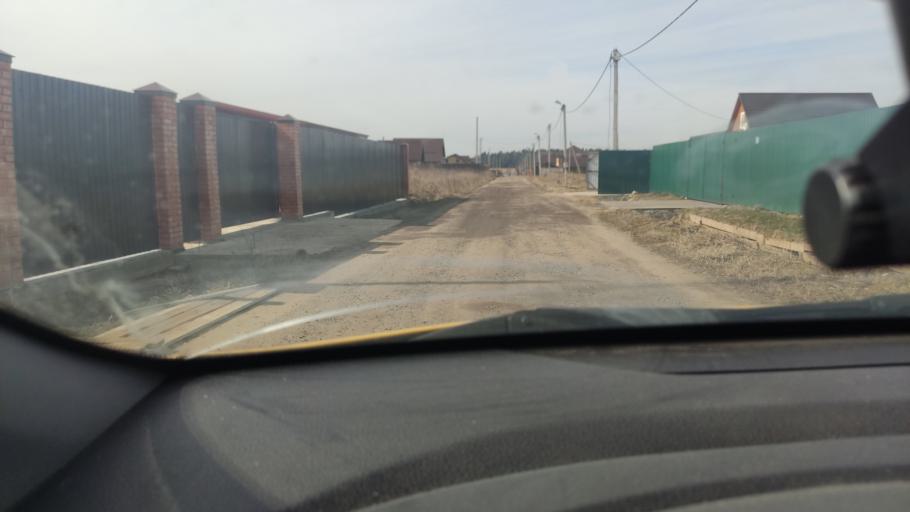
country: RU
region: Moskovskaya
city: Ruza
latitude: 55.7632
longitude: 36.1353
